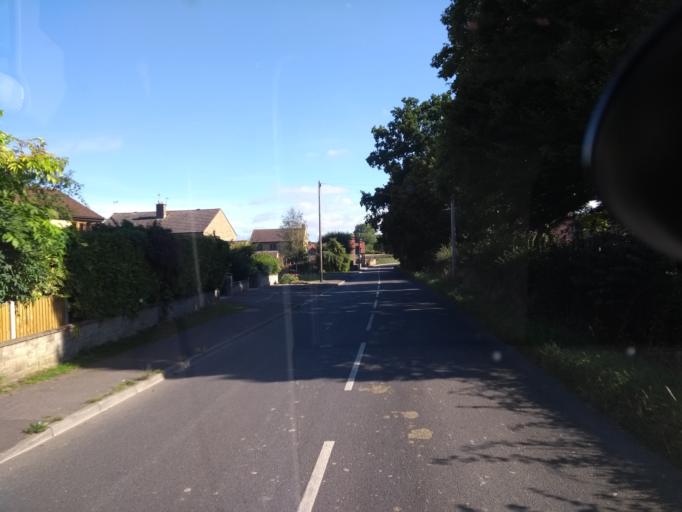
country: GB
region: England
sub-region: Somerset
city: Martock
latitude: 50.9799
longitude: -2.7661
